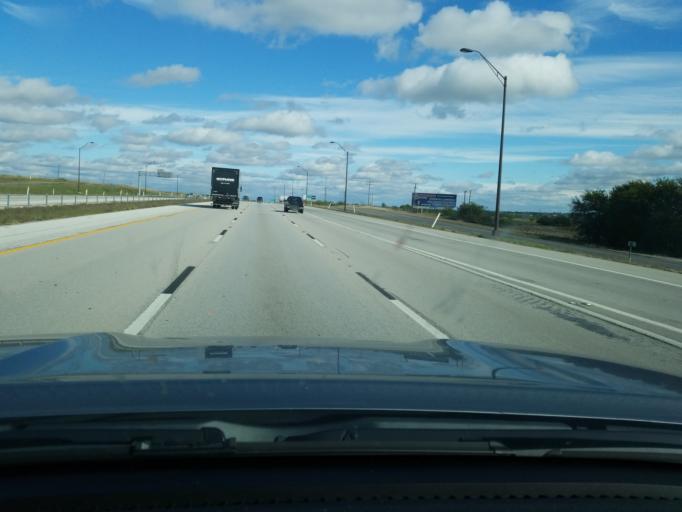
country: US
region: Texas
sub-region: Parker County
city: Aledo
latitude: 32.7207
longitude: -97.5514
